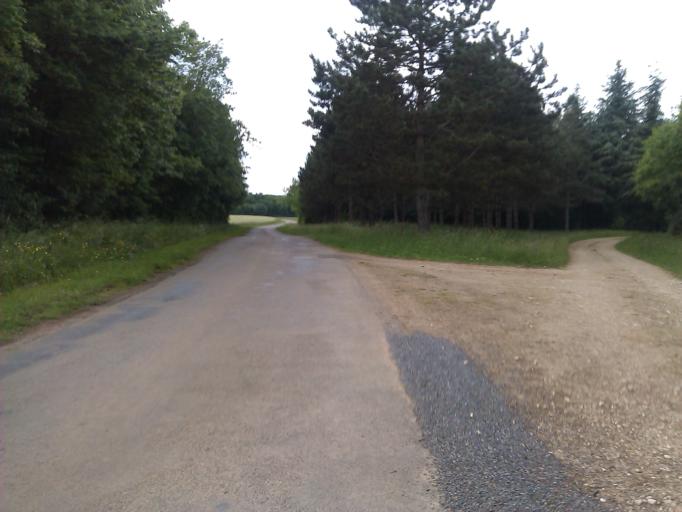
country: FR
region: Poitou-Charentes
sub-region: Departement de la Charente
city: Nanteuil-en-Vallee
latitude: 45.9599
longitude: 0.2770
